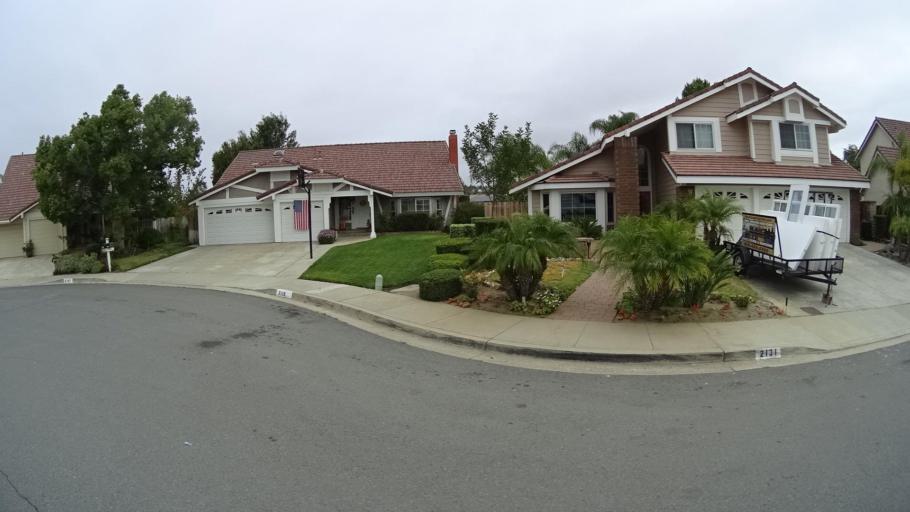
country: US
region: California
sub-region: San Diego County
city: Rancho San Diego
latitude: 32.7588
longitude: -116.9091
